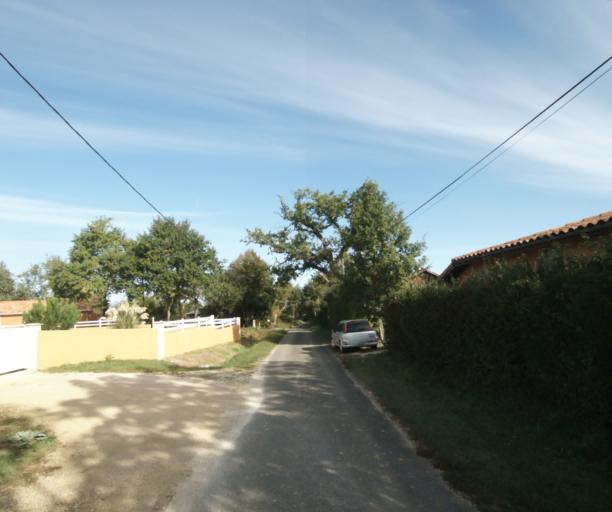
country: FR
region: Midi-Pyrenees
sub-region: Departement du Gers
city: Eauze
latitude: 43.8913
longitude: 0.1326
